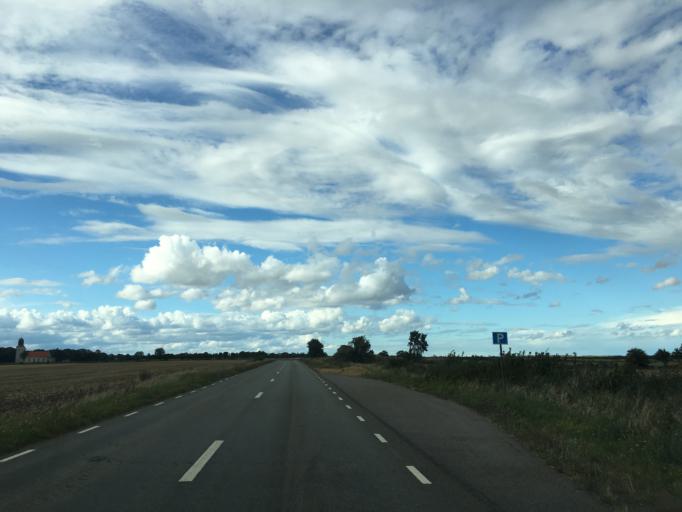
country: SE
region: Kalmar
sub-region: Morbylanga Kommun
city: Moerbylanga
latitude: 56.4009
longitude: 16.4367
